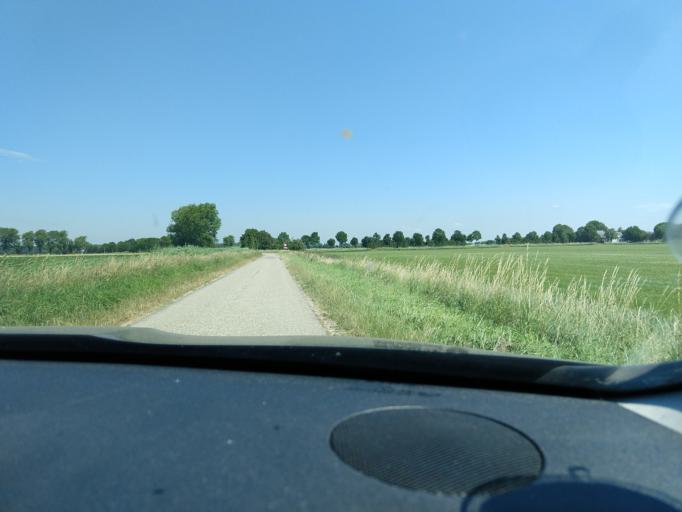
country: NL
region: Zeeland
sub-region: Gemeente Veere
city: Veere
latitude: 51.5150
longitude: 3.6654
